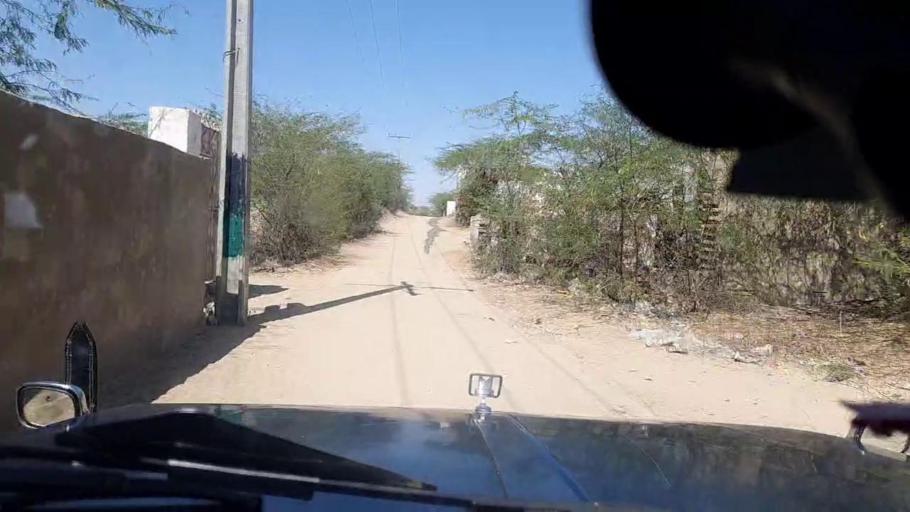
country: PK
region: Sindh
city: Mithi
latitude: 24.5947
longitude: 69.7100
